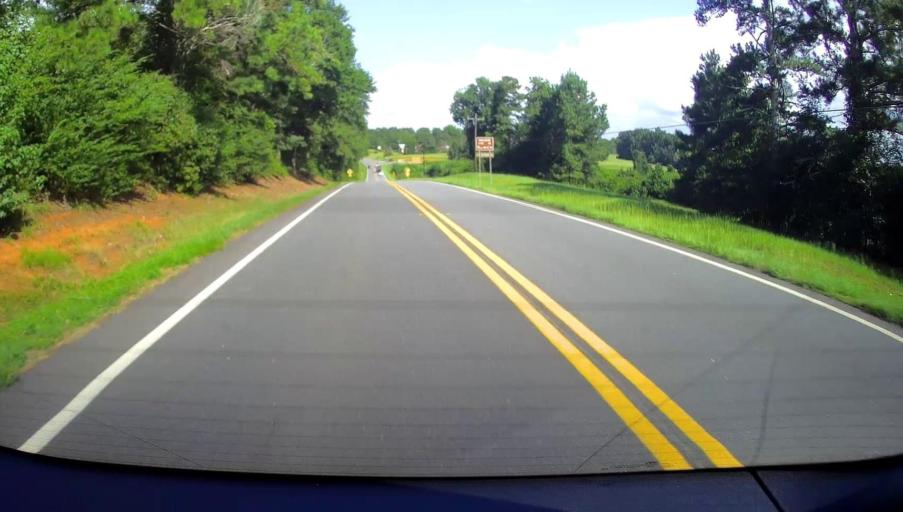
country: US
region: Georgia
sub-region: Upson County
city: Hannahs Mill
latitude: 32.8998
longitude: -84.4166
